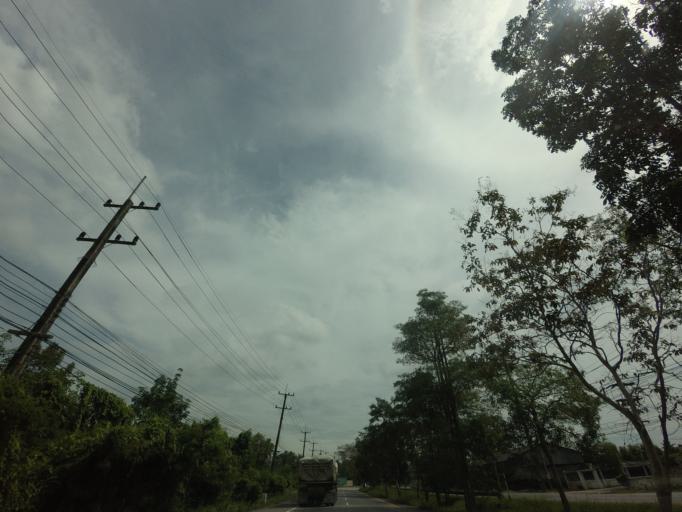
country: TH
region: Rayong
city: Klaeng
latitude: 12.7118
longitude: 101.5571
